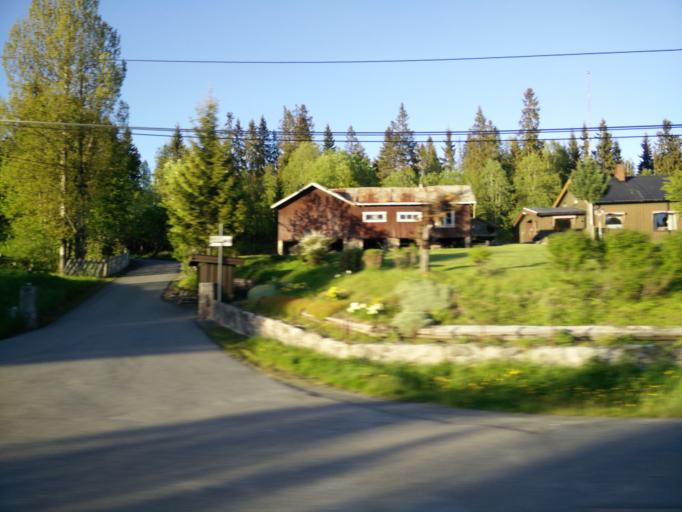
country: NO
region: Akershus
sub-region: Baerum
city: Skui
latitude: 59.9613
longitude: 10.3587
